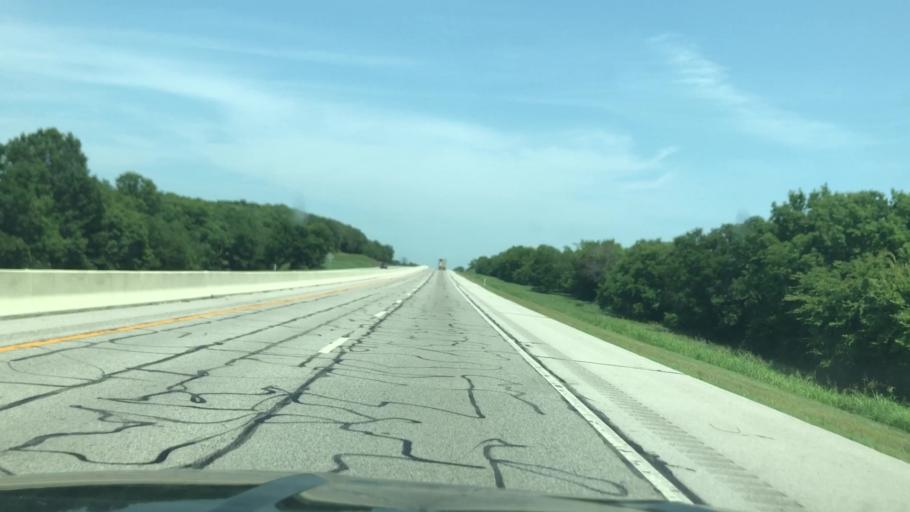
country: US
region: Oklahoma
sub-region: Rogers County
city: Chelsea
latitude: 36.4570
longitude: -95.3554
